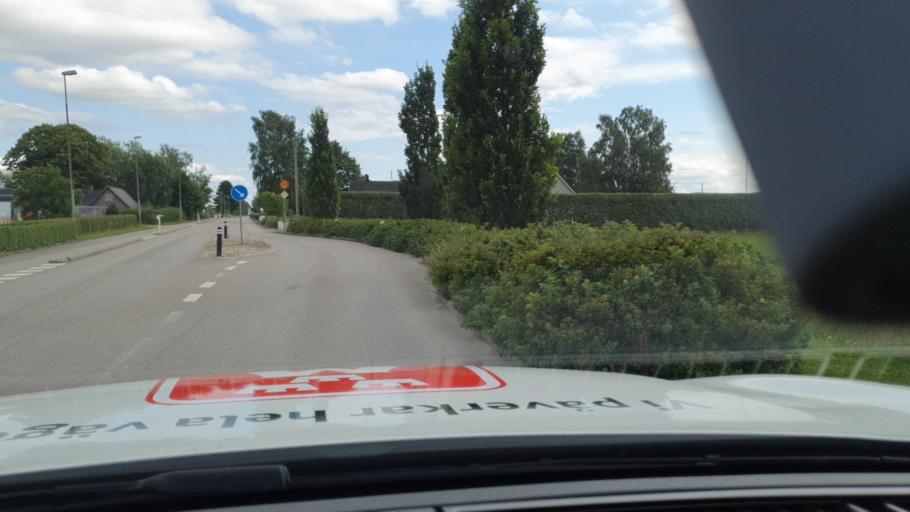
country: SE
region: Skane
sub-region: Astorps Kommun
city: Kvidinge
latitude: 56.1312
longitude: 13.0647
